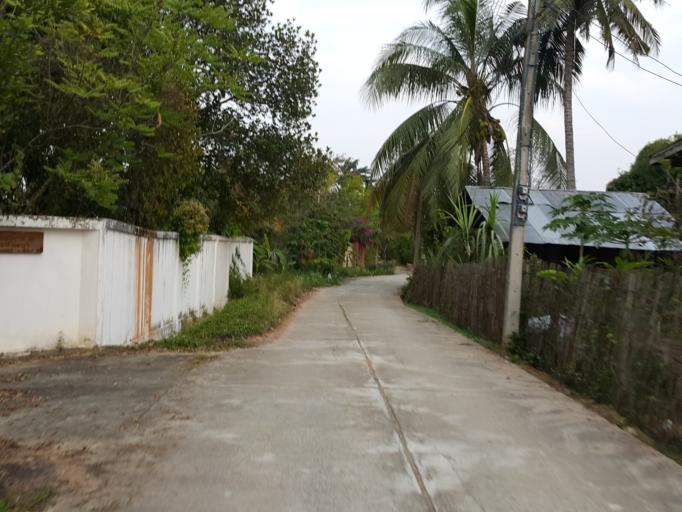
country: TH
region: Chiang Mai
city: San Sai
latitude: 18.8937
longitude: 99.1361
